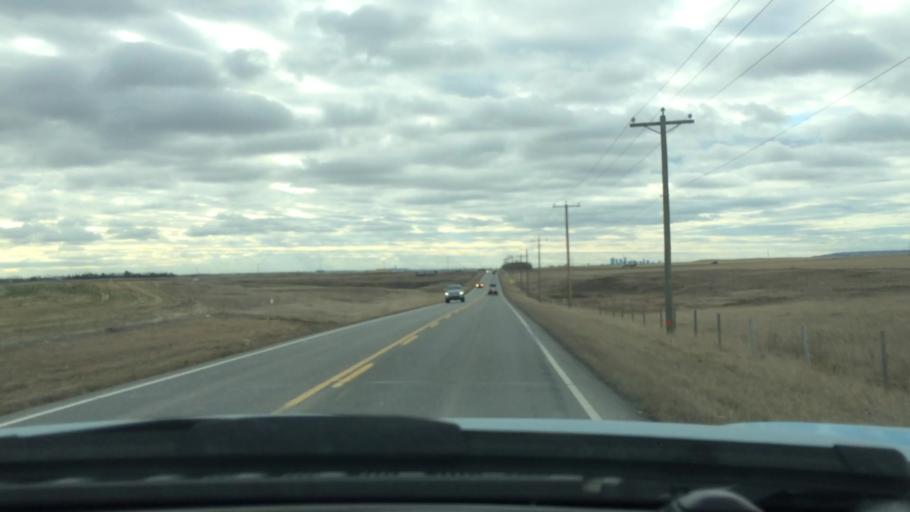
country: CA
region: Alberta
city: Airdrie
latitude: 51.2185
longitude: -114.0250
